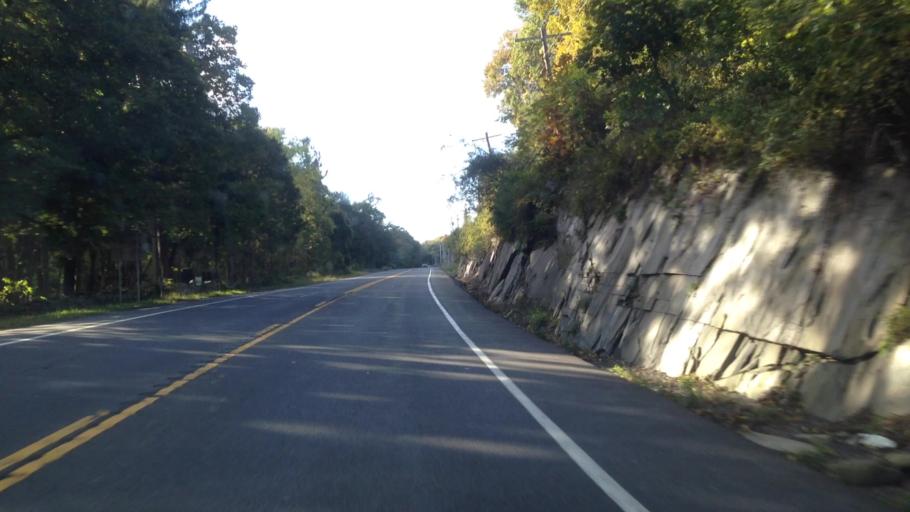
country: US
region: New York
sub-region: Dutchess County
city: Hyde Park
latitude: 41.7845
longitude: -73.9595
